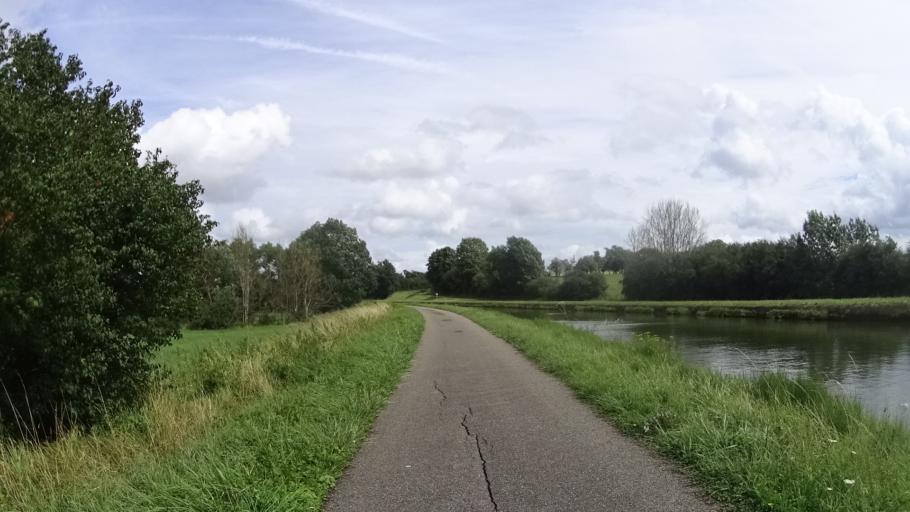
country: FR
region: Lorraine
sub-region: Departement de la Moselle
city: Lorquin
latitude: 48.6822
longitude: 6.9356
